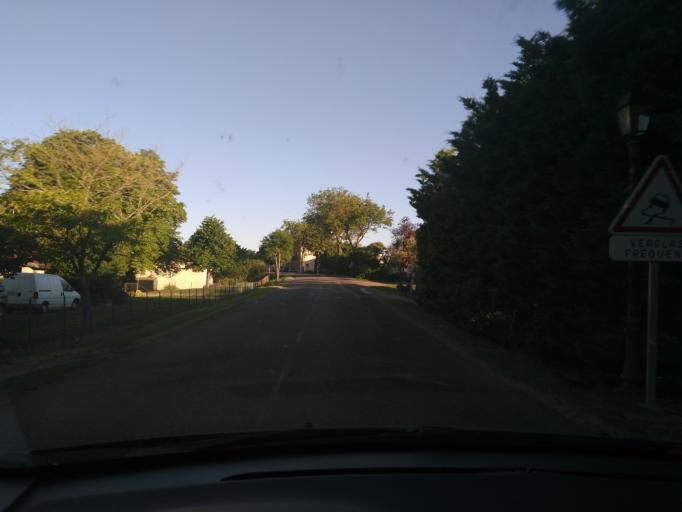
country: FR
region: Midi-Pyrenees
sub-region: Departement du Gers
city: Jegun
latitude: 43.8525
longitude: 0.5303
